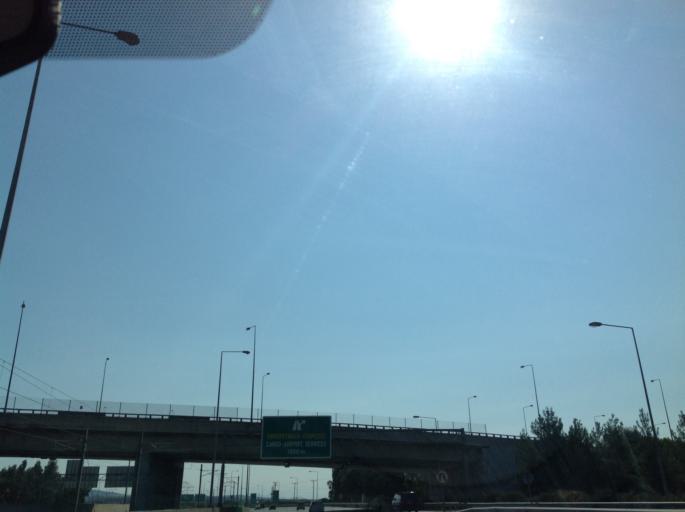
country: GR
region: Attica
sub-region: Nomarchia Anatolikis Attikis
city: Markopoulo
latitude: 37.9142
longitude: 23.9193
